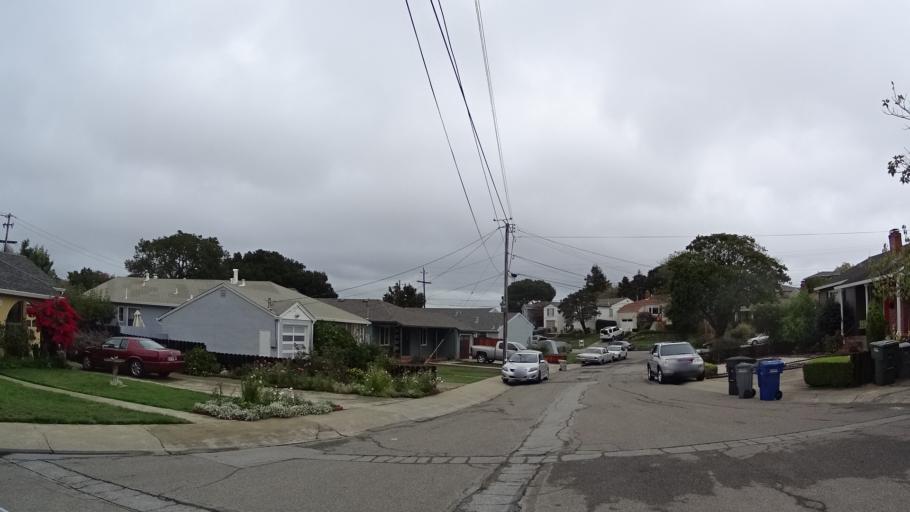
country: US
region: California
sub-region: San Mateo County
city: San Bruno
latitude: 37.6099
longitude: -122.4169
